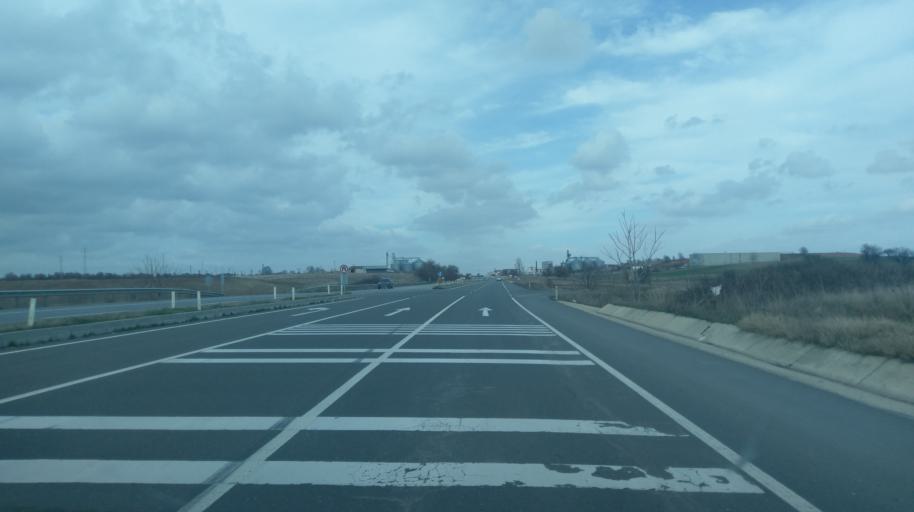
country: TR
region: Edirne
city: Hamidiye
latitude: 41.1994
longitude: 26.6734
